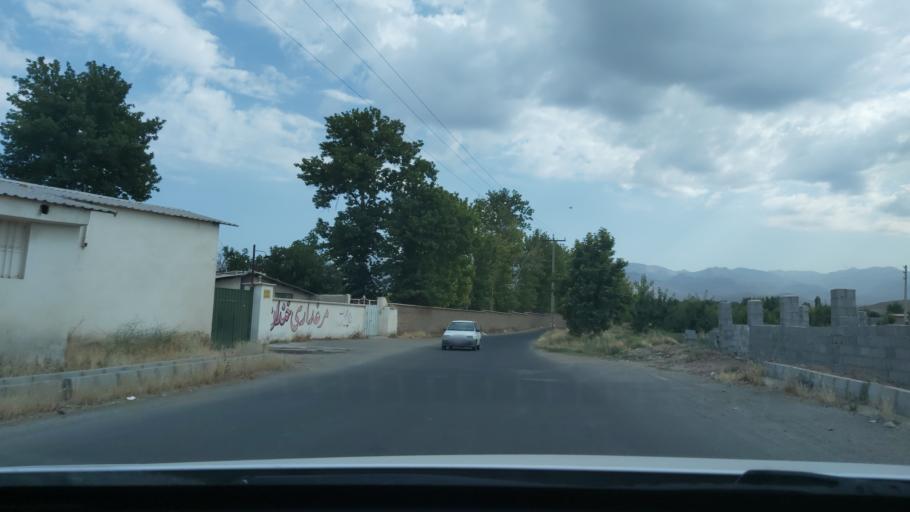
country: IR
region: Alborz
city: Hashtgerd
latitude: 35.9472
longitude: 50.7725
